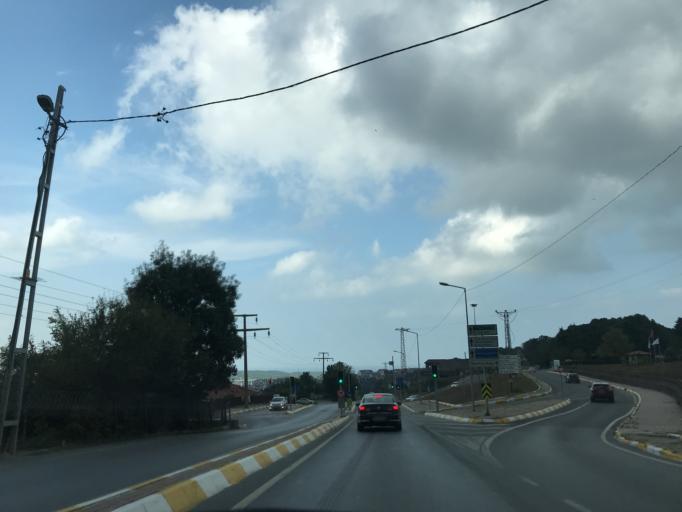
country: TR
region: Istanbul
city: Arikoey
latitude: 41.2040
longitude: 29.0404
